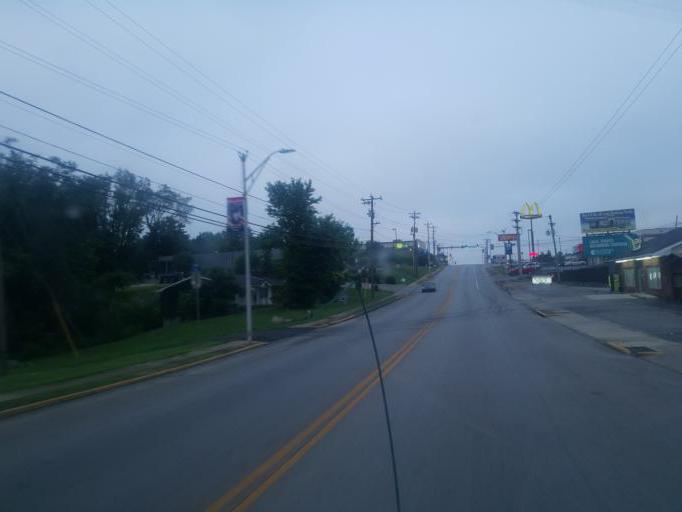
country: US
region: Kentucky
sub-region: Clinton County
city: Albany
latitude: 36.6978
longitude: -85.1354
